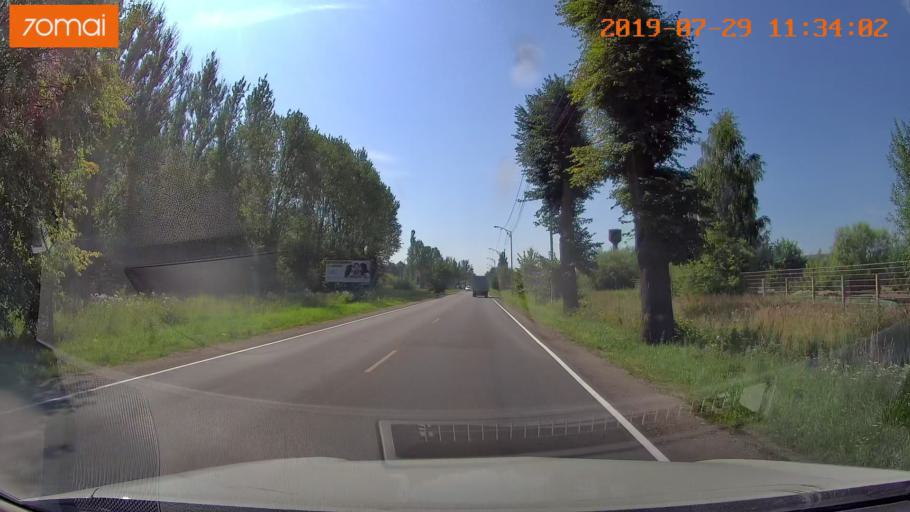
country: RU
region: Kaliningrad
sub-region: Gorod Kaliningrad
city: Kaliningrad
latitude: 54.6593
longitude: 20.5414
